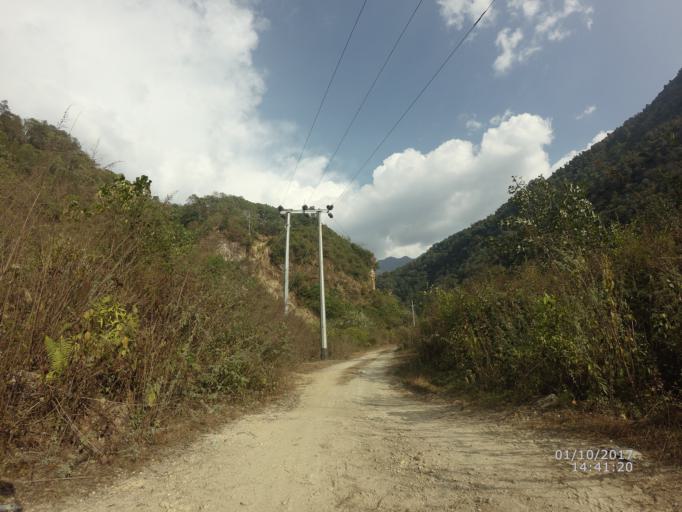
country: NP
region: Western Region
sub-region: Gandaki Zone
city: Pokhara
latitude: 28.3453
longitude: 83.9741
